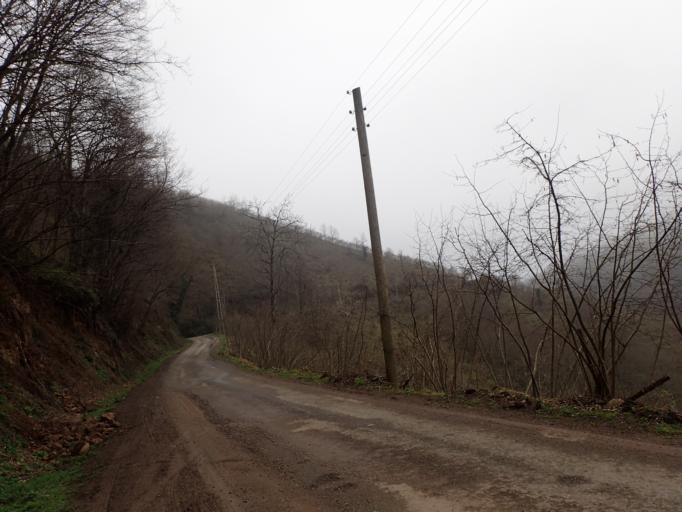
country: TR
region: Ordu
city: Camas
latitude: 40.9258
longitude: 37.5519
